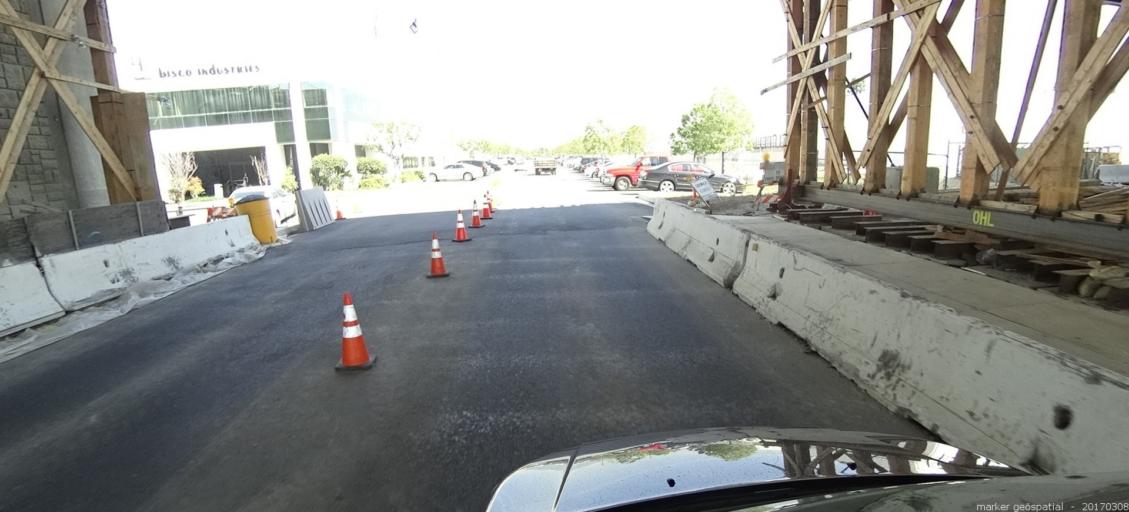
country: US
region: California
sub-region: Orange County
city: Yorba Linda
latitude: 33.8657
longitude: -117.8186
